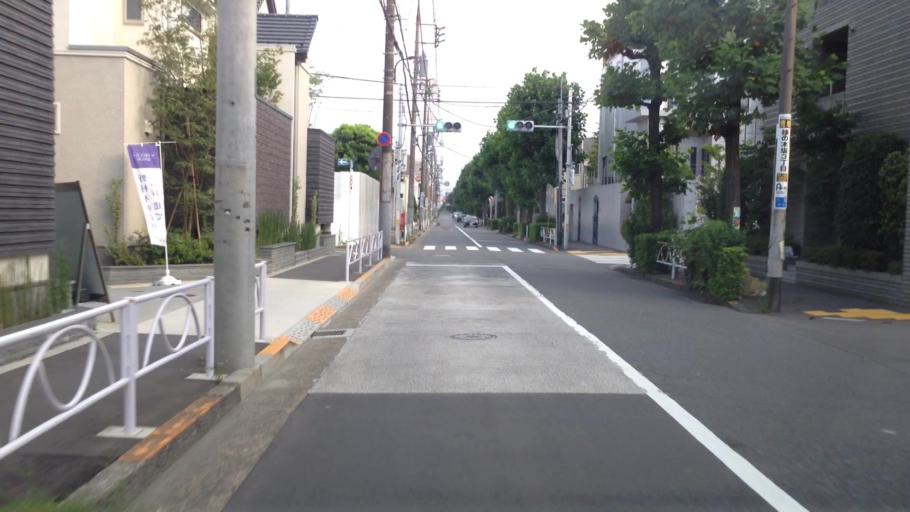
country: JP
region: Tokyo
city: Tokyo
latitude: 35.6252
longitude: 139.6726
